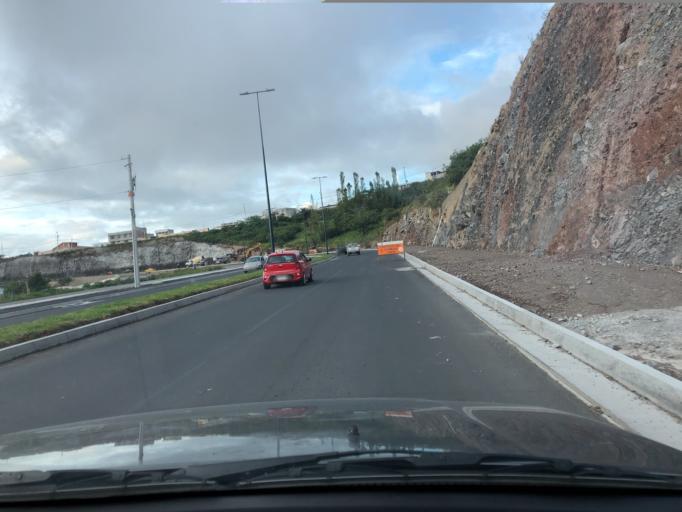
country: EC
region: Imbabura
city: Ibarra
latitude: 0.3477
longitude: -78.1428
